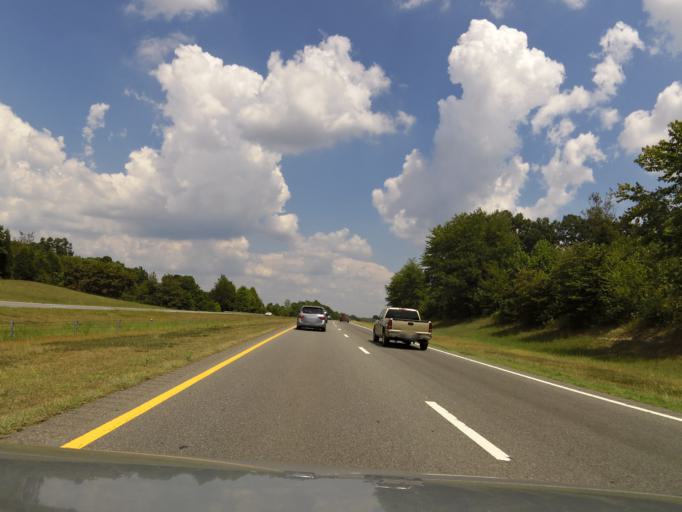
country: US
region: North Carolina
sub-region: Cleveland County
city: White Plains
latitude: 35.2533
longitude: -81.3964
